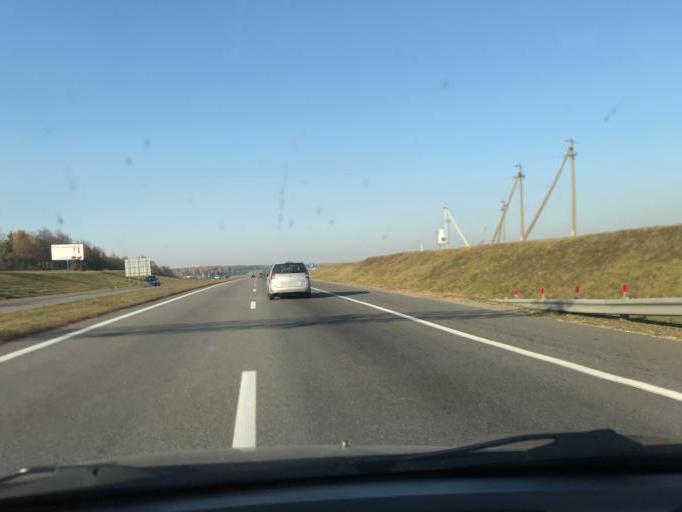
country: BY
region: Minsk
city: Samakhvalavichy
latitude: 53.7334
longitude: 27.5171
